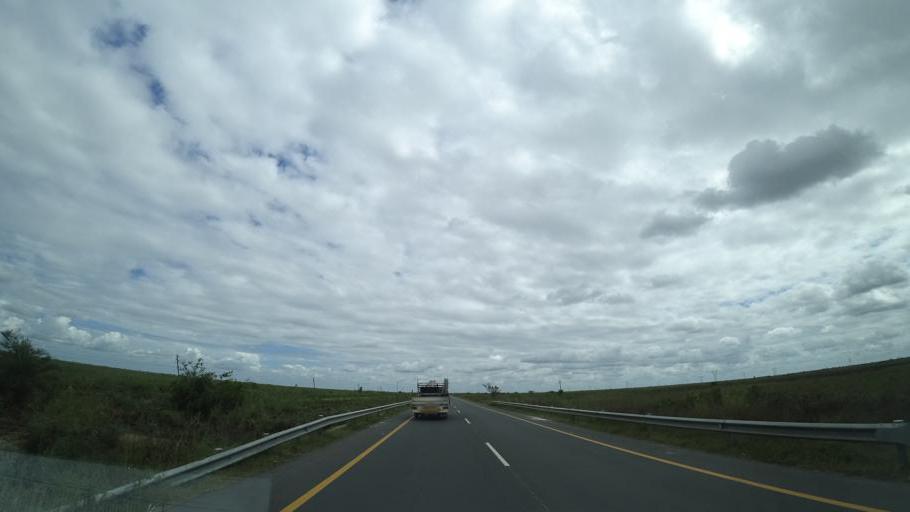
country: MZ
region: Sofala
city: Dondo
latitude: -19.4911
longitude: 34.5859
